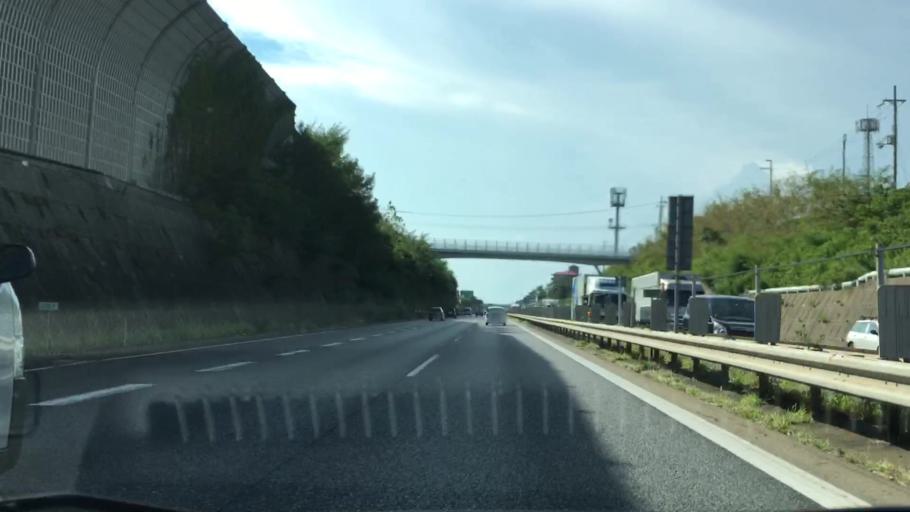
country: JP
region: Hyogo
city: Akashi
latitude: 34.7058
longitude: 134.9527
